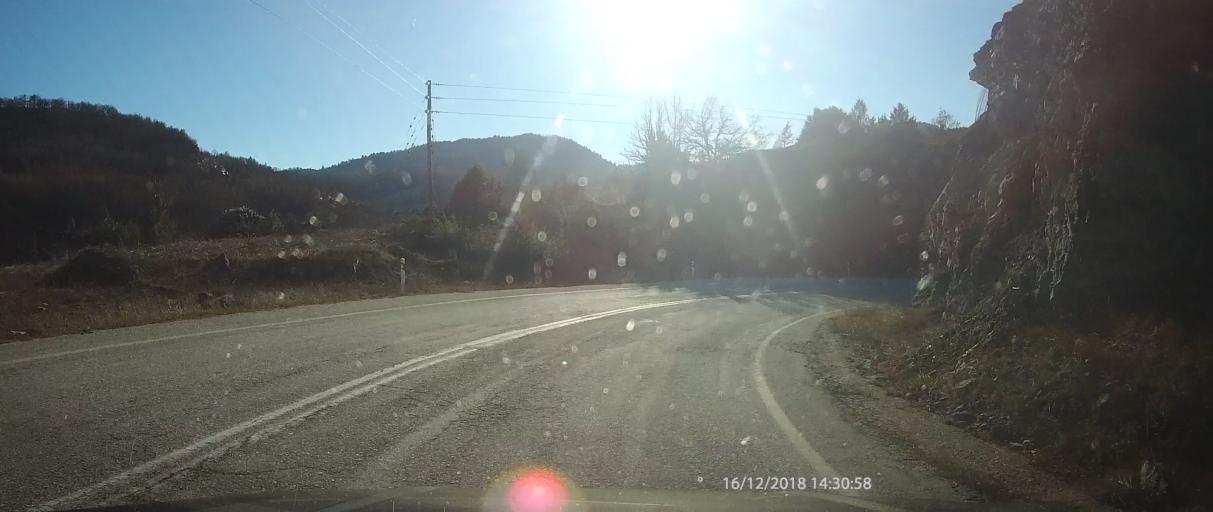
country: GR
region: West Macedonia
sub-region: Nomos Kozanis
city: Tsotili
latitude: 40.1933
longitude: 21.1865
